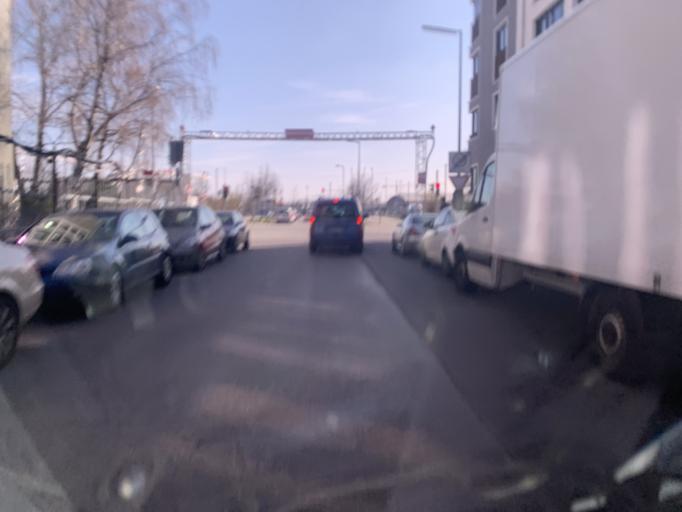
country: DE
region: Bavaria
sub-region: Upper Bavaria
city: Bogenhausen
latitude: 48.1386
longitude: 11.6200
